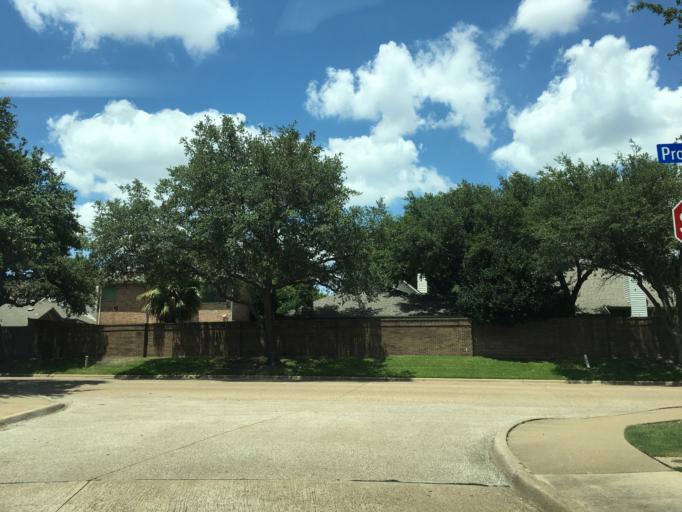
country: US
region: Texas
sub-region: Dallas County
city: Addison
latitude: 32.9454
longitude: -96.8470
